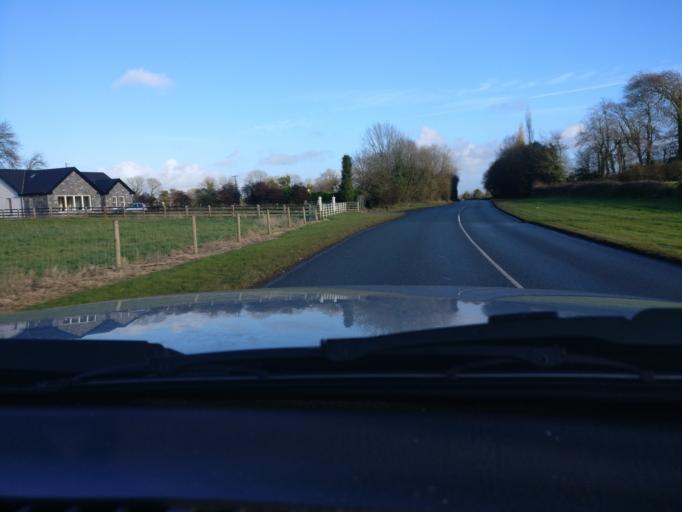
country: IE
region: Leinster
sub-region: An Iarmhi
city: An Muileann gCearr
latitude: 53.5152
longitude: -7.3863
